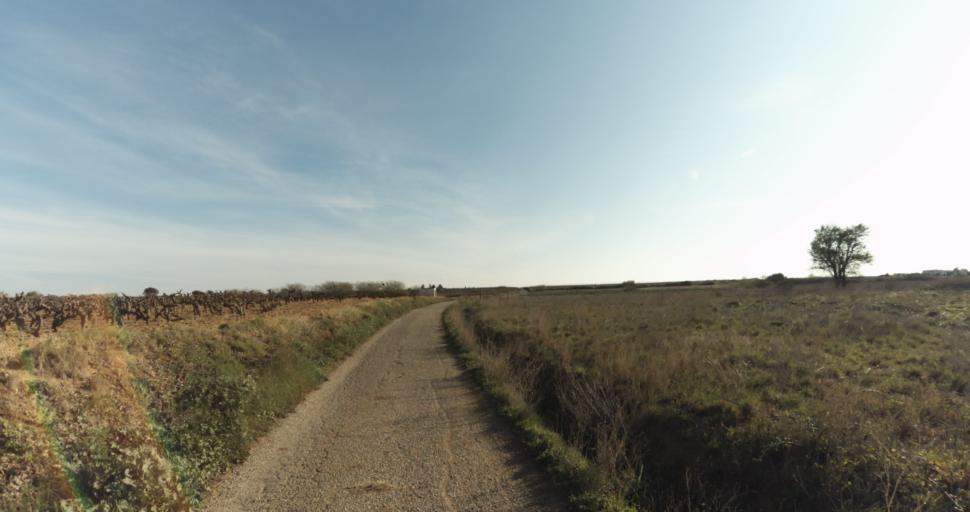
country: FR
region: Languedoc-Roussillon
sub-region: Departement de l'Herault
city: Marseillan
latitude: 43.3604
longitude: 3.5067
